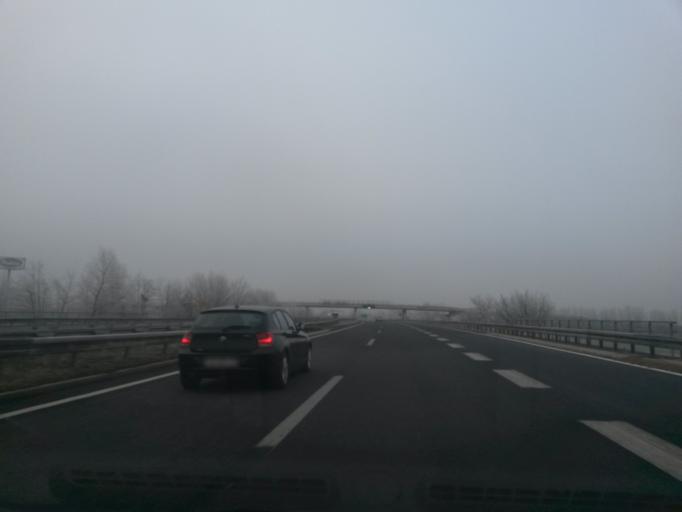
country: HR
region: Zagrebacka
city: Brckovljani
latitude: 45.9073
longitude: 16.2739
